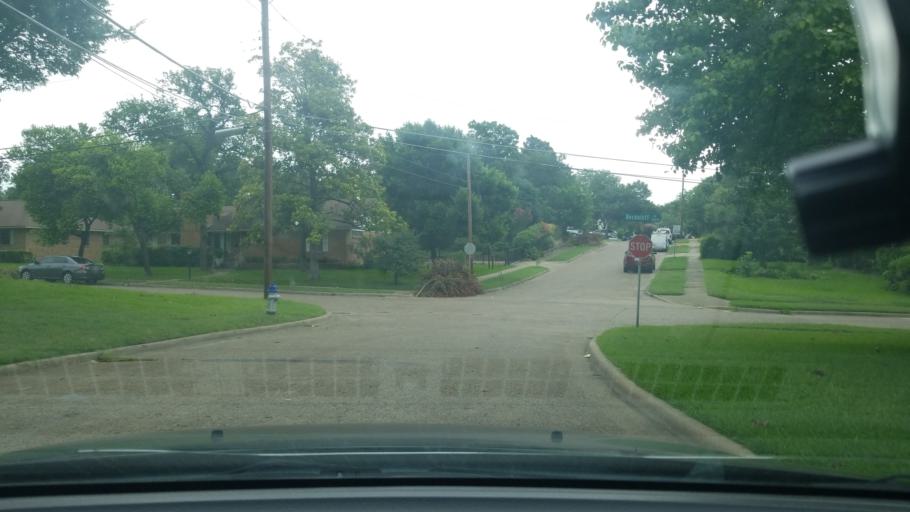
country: US
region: Texas
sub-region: Dallas County
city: Balch Springs
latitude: 32.7696
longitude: -96.6936
